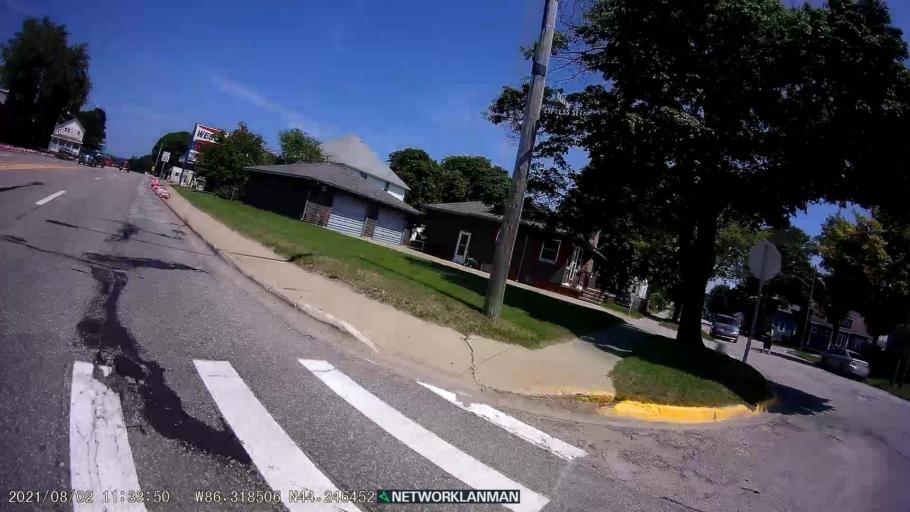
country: US
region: Michigan
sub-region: Manistee County
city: Manistee
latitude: 44.2463
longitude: -86.3185
